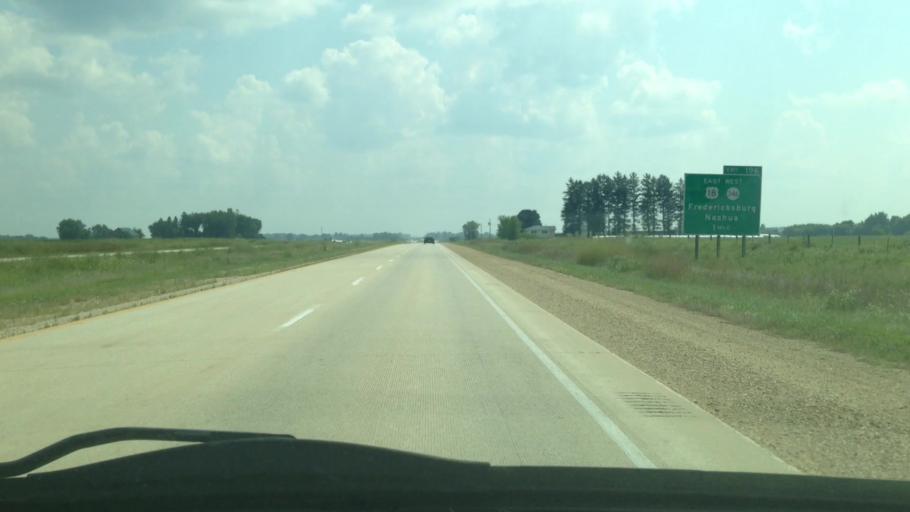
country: US
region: Iowa
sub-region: Chickasaw County
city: New Hampton
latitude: 42.9851
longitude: -92.3178
